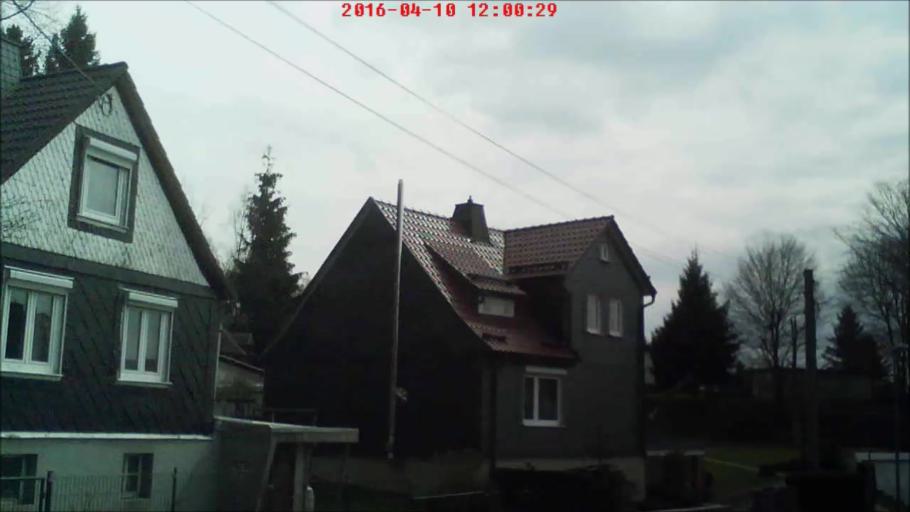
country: DE
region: Thuringia
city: Zella-Mehlis
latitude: 50.6699
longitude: 10.6653
